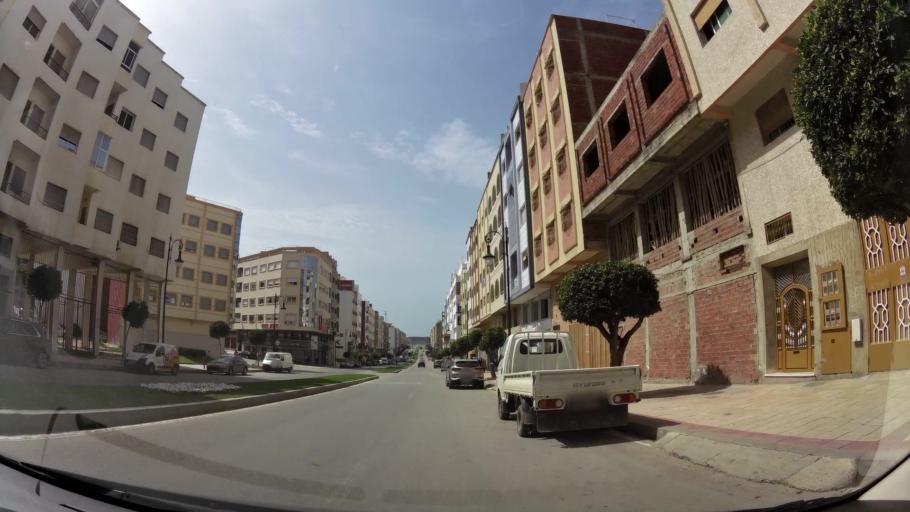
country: MA
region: Tanger-Tetouan
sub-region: Tanger-Assilah
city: Tangier
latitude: 35.7443
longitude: -5.8319
